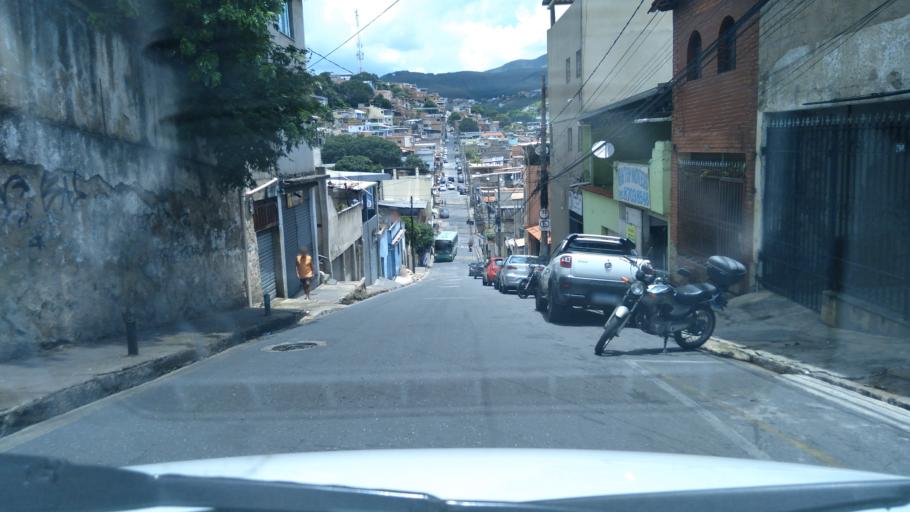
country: BR
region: Minas Gerais
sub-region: Belo Horizonte
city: Belo Horizonte
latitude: -19.9088
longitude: -43.8925
